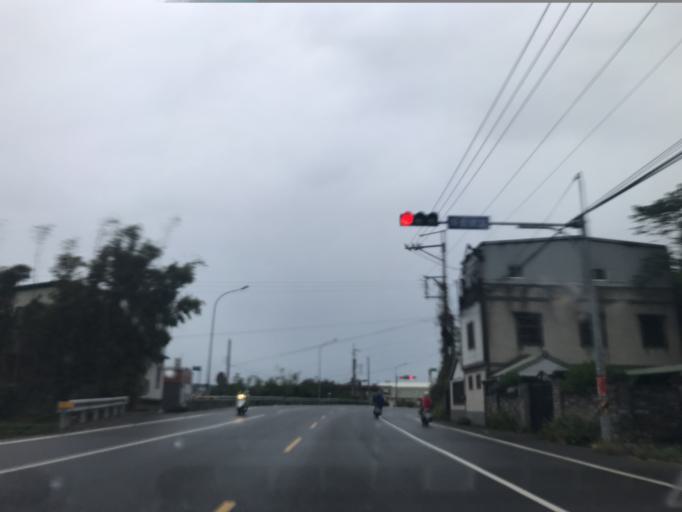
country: TW
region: Taiwan
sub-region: Hsinchu
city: Zhubei
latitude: 24.8362
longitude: 121.0956
